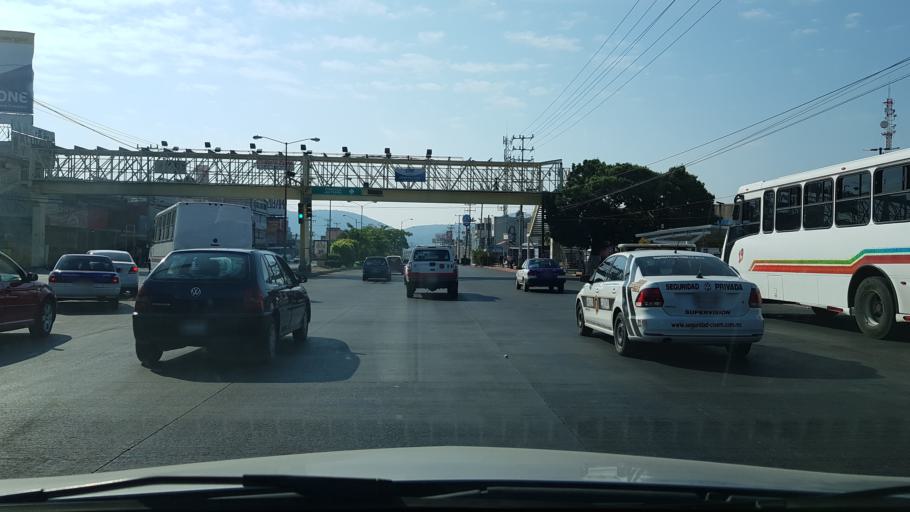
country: MX
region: Morelos
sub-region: Jiutepec
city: Jiutepec
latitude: 18.9026
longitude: -99.1745
